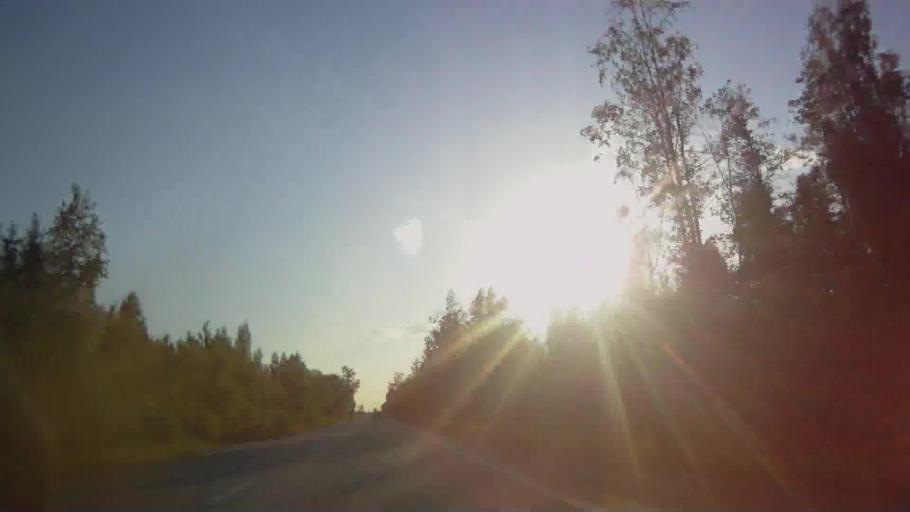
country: LV
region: Livani
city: Livani
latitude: 56.5305
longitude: 26.3570
